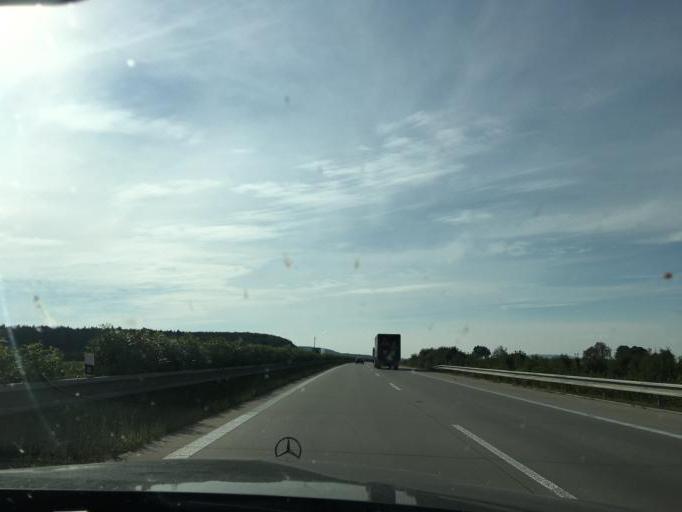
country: CZ
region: Central Bohemia
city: Zizelice
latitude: 50.1291
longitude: 15.3430
